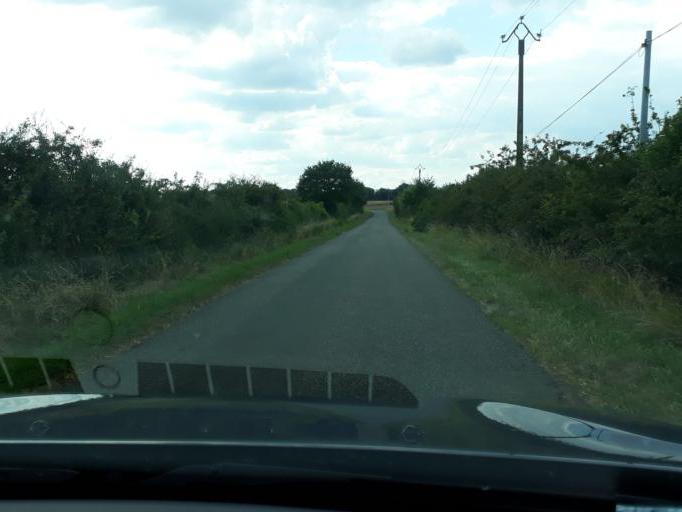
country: FR
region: Centre
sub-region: Departement du Cher
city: Jouet-sur-l'Aubois
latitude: 46.9841
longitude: 2.9254
